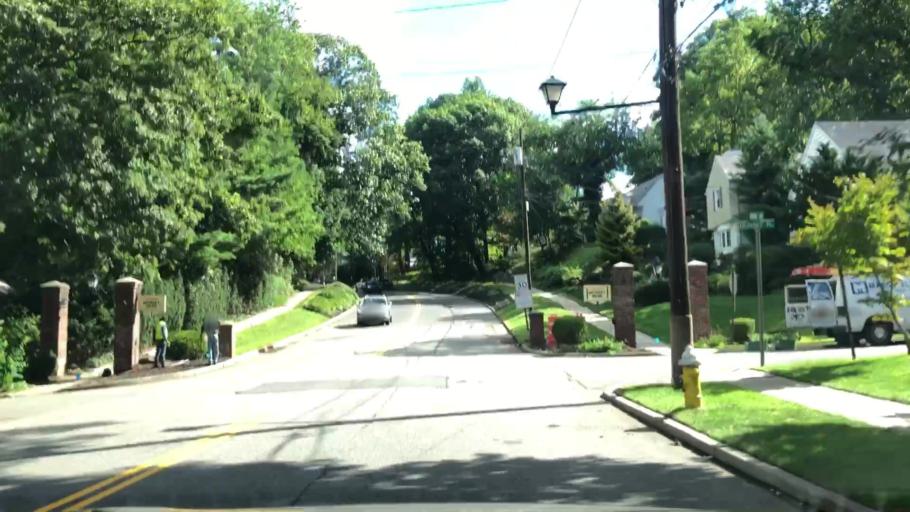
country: US
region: New York
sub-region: Nassau County
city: Manhasset
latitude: 40.7977
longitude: -73.6935
